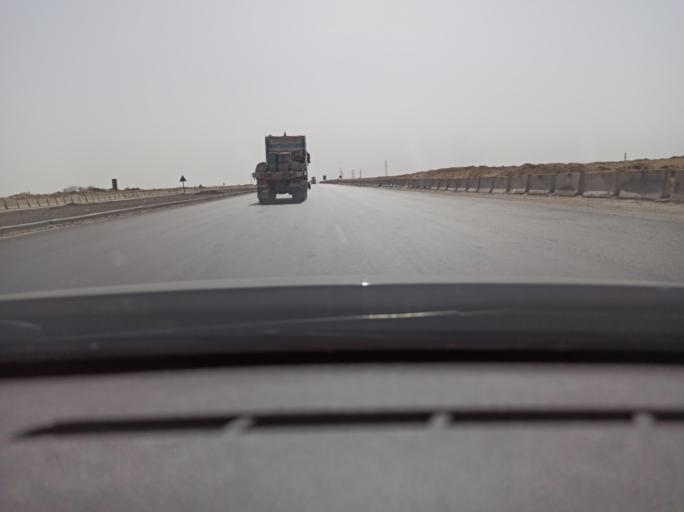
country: EG
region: Muhafazat al Qahirah
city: Halwan
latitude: 29.7875
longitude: 31.3504
